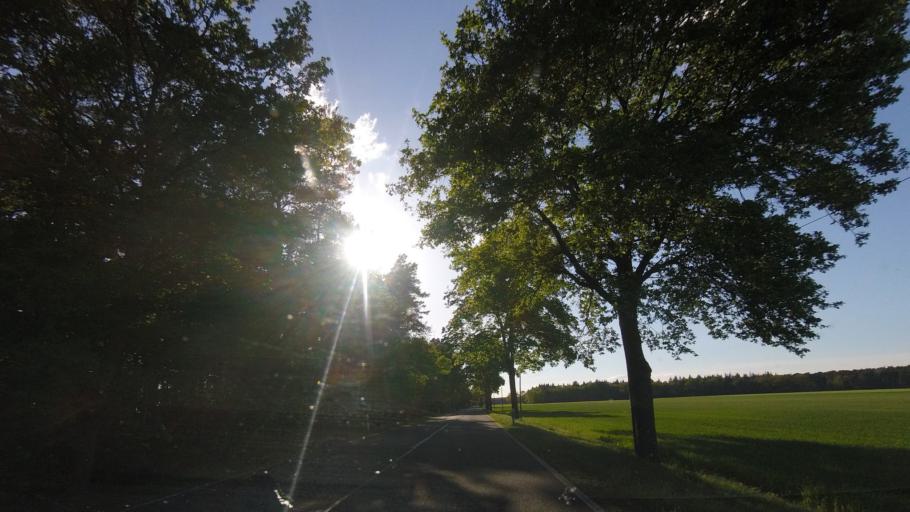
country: DE
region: Brandenburg
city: Kasel-Golzig
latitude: 51.9676
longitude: 13.6929
